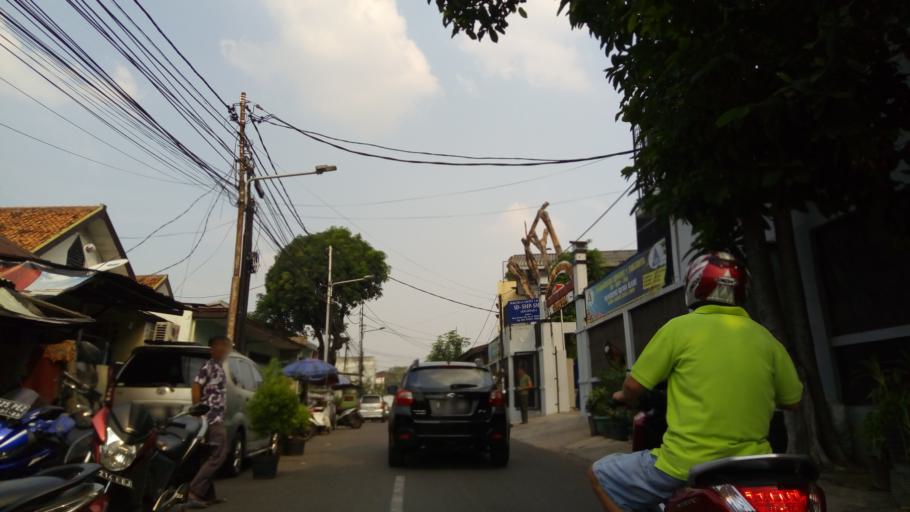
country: ID
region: Jakarta Raya
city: Jakarta
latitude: -6.1789
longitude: 106.8436
